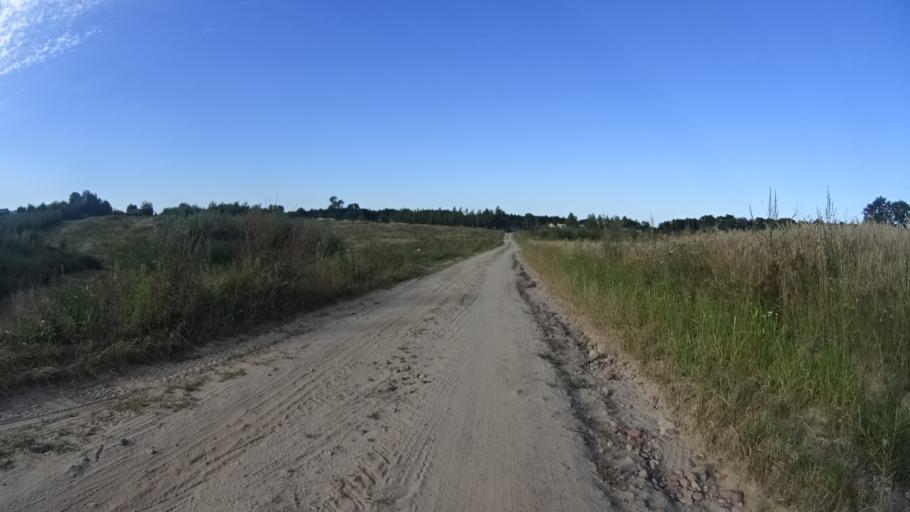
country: PL
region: Masovian Voivodeship
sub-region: Powiat grojecki
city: Goszczyn
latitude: 51.6903
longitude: 20.8141
